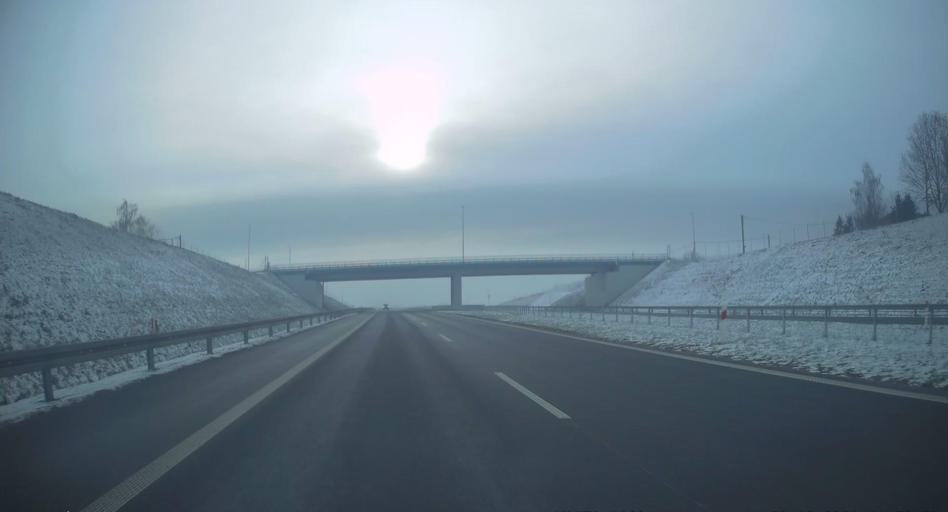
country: PL
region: Lesser Poland Voivodeship
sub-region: Powiat krakowski
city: Slomniki
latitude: 50.2736
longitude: 20.0206
